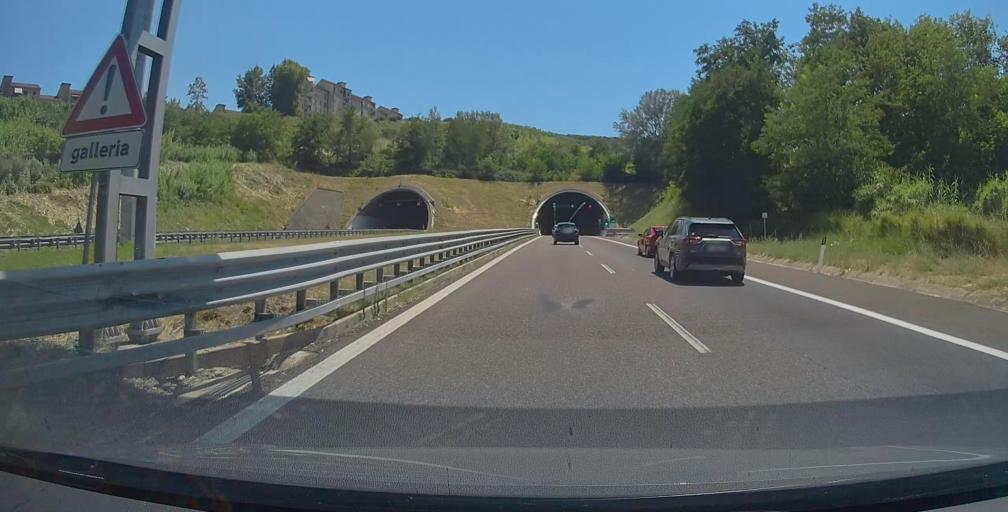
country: IT
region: Calabria
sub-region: Provincia di Cosenza
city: Cosenza
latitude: 39.3100
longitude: 16.2369
